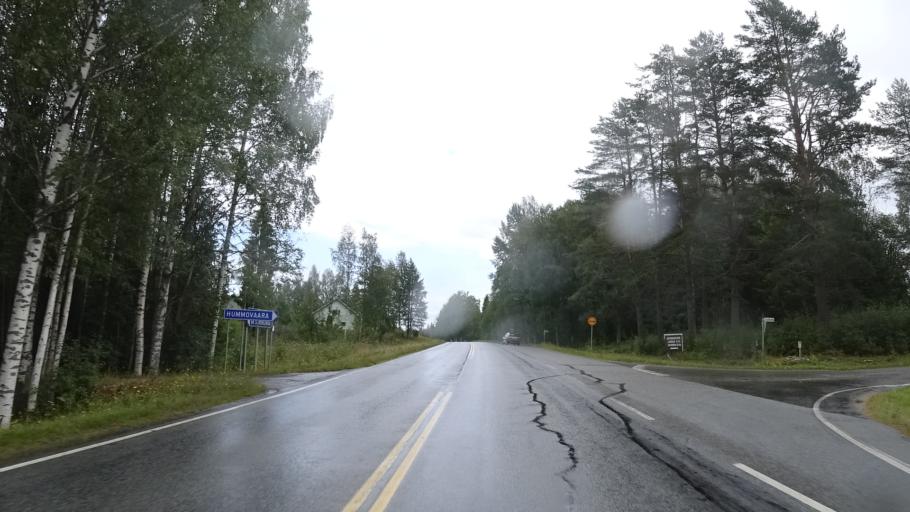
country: FI
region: North Karelia
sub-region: Keski-Karjala
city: Raeaekkylae
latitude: 62.0777
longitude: 29.6501
